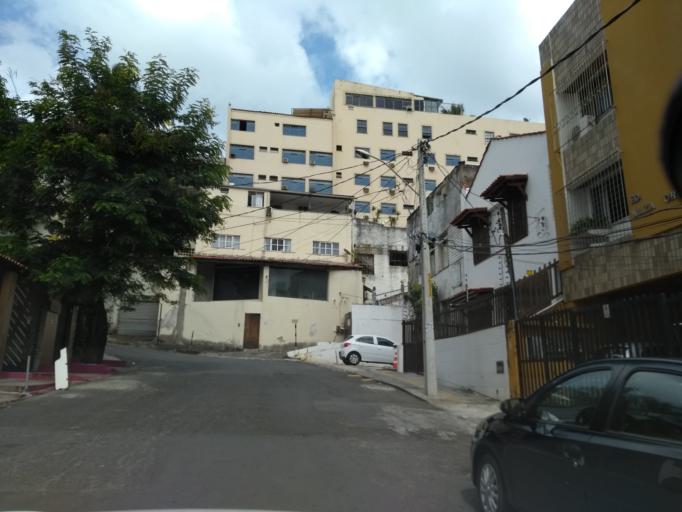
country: BR
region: Bahia
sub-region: Salvador
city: Salvador
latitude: -13.0071
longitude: -38.5279
